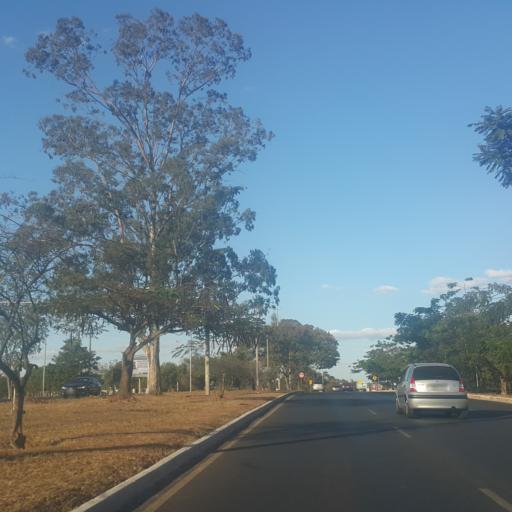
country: BR
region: Federal District
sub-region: Brasilia
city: Brasilia
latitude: -15.8362
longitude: -47.9719
